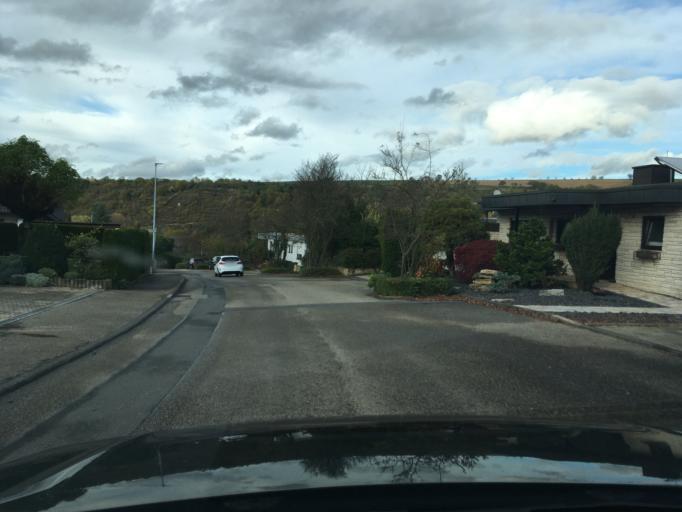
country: DE
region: Baden-Wuerttemberg
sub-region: Regierungsbezirk Stuttgart
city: Mockmuhl
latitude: 49.3198
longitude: 9.3730
